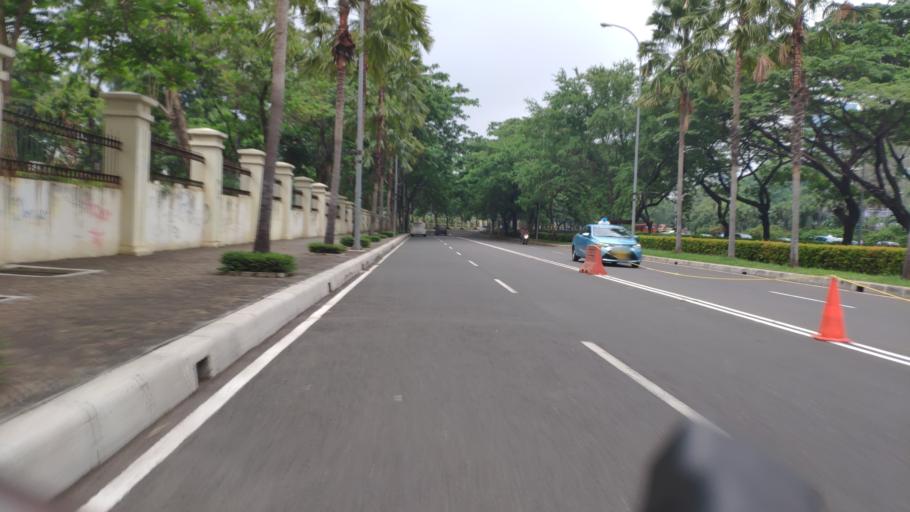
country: ID
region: Jakarta Raya
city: Jakarta
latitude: -6.2207
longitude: 106.8359
